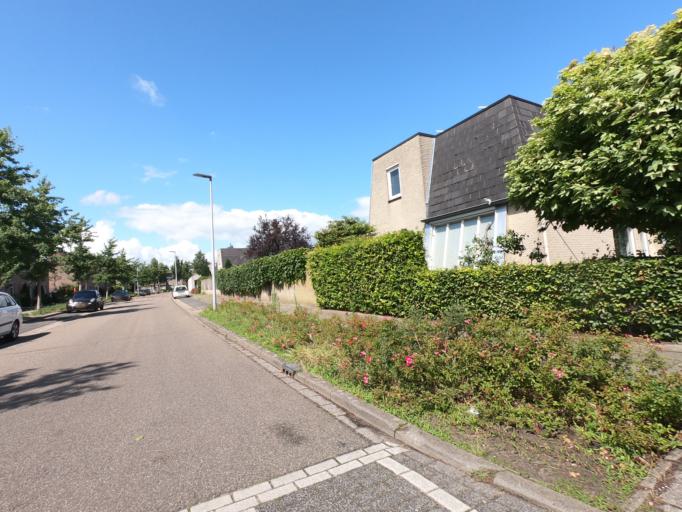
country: NL
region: North Brabant
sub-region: Gemeente Uden
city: Uden
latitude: 51.6513
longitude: 5.6181
